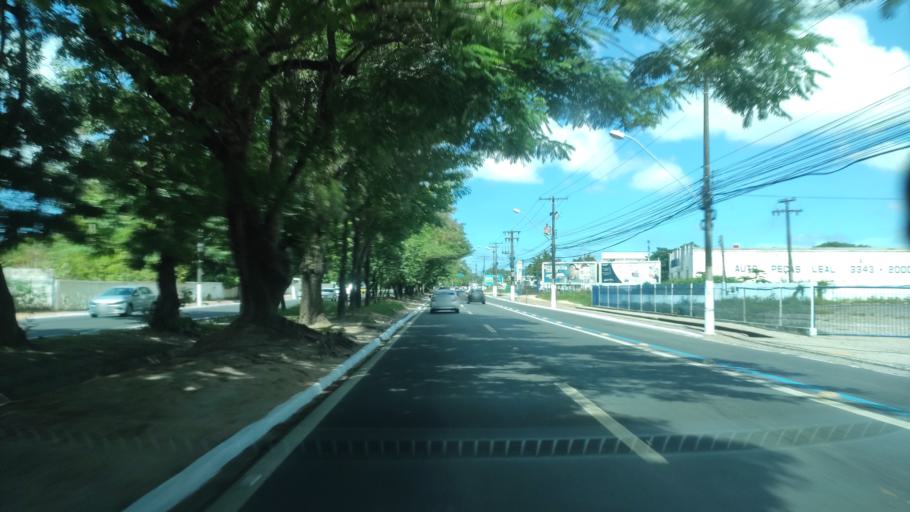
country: BR
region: Alagoas
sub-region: Maceio
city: Maceio
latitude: -9.5932
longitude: -35.7550
